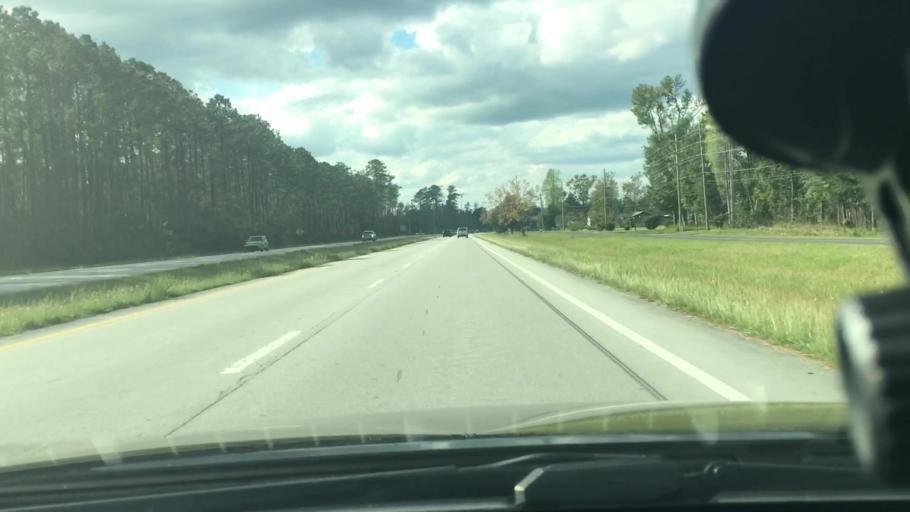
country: US
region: North Carolina
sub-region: Craven County
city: Neuse Forest
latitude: 34.9668
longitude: -76.9643
